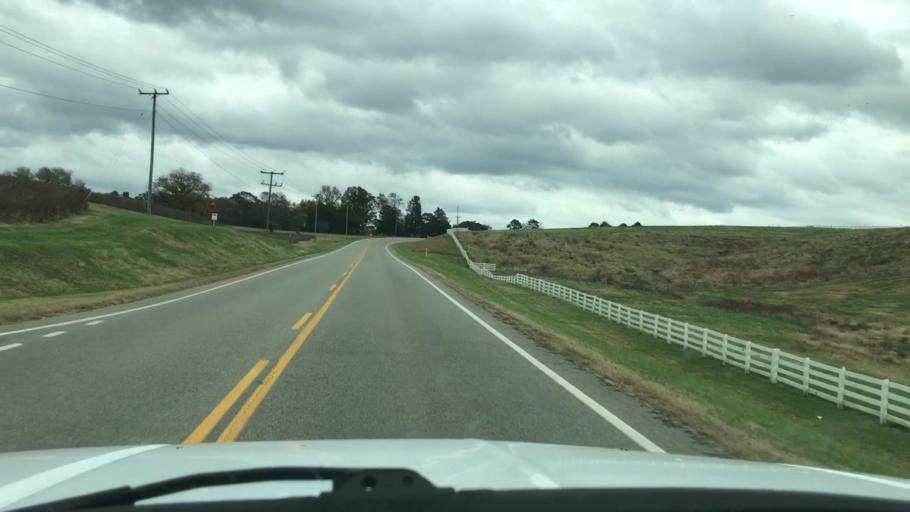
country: US
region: Virginia
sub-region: Goochland County
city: Goochland
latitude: 37.6466
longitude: -77.8221
